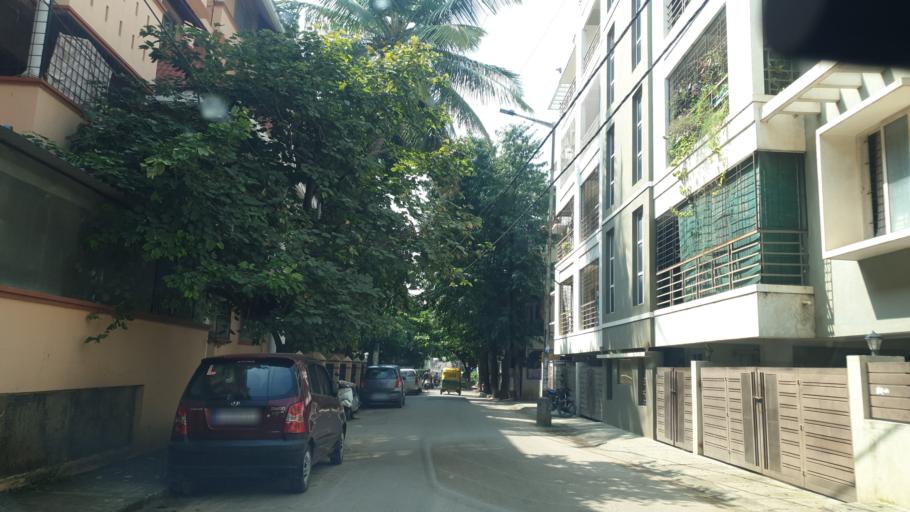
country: IN
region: Karnataka
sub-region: Bangalore Urban
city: Bangalore
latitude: 12.9696
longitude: 77.6657
